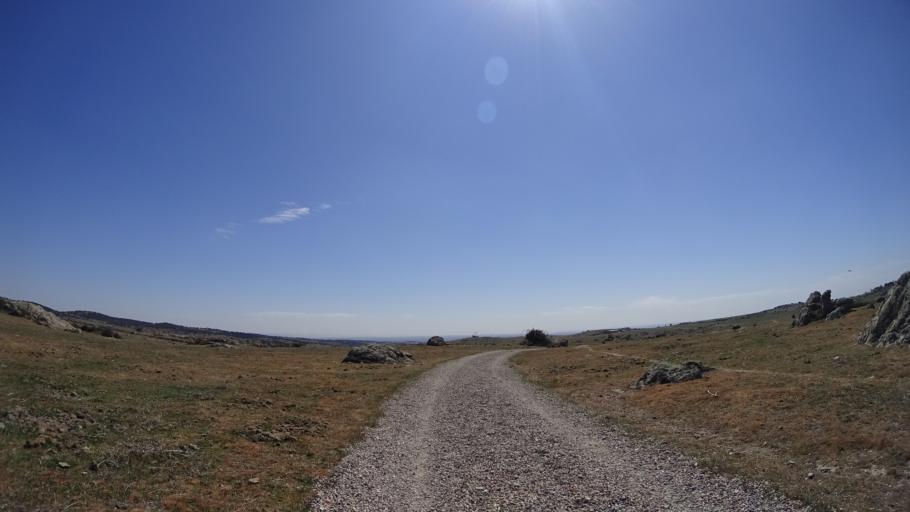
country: ES
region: Madrid
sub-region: Provincia de Madrid
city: Colmenar Viejo
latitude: 40.7029
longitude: -3.7518
